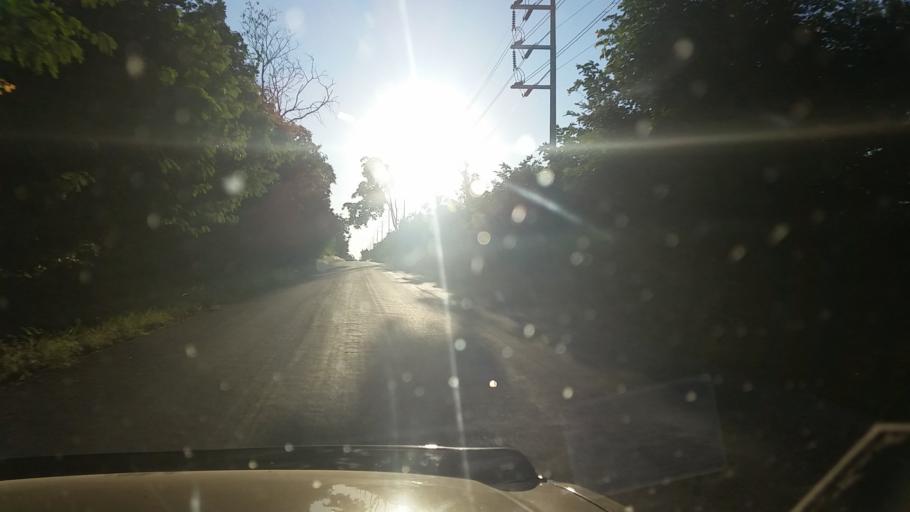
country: TH
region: Chaiyaphum
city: Sap Yai
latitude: 15.6646
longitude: 101.6669
